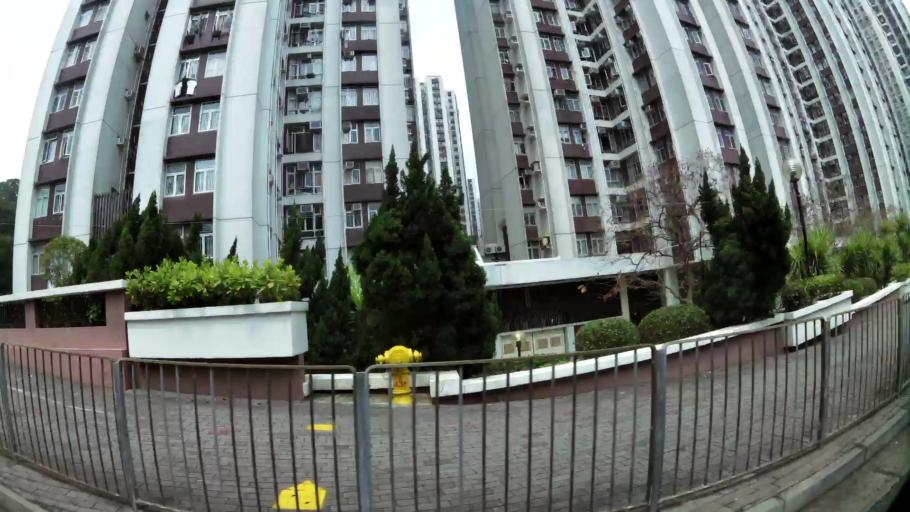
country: HK
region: Wanchai
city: Wan Chai
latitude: 22.2854
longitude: 114.2209
